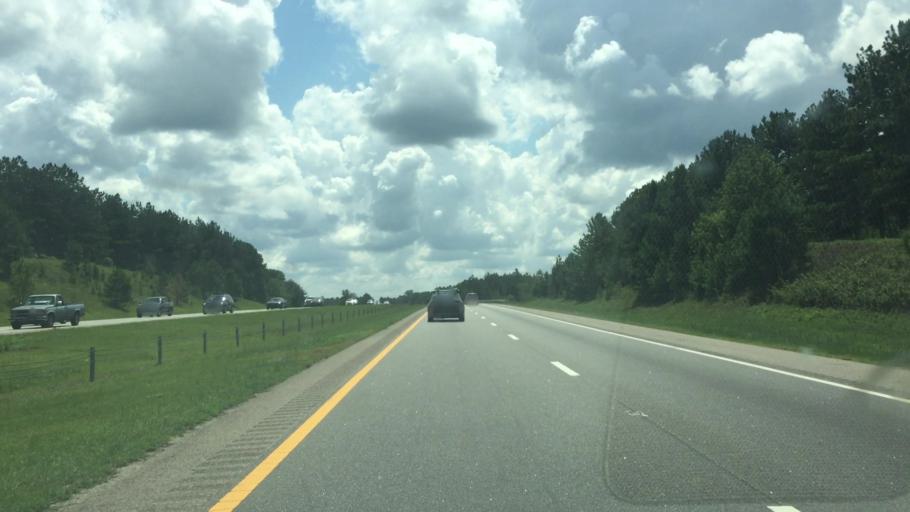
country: US
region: North Carolina
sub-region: Richmond County
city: East Rockingham
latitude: 34.8756
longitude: -79.7699
